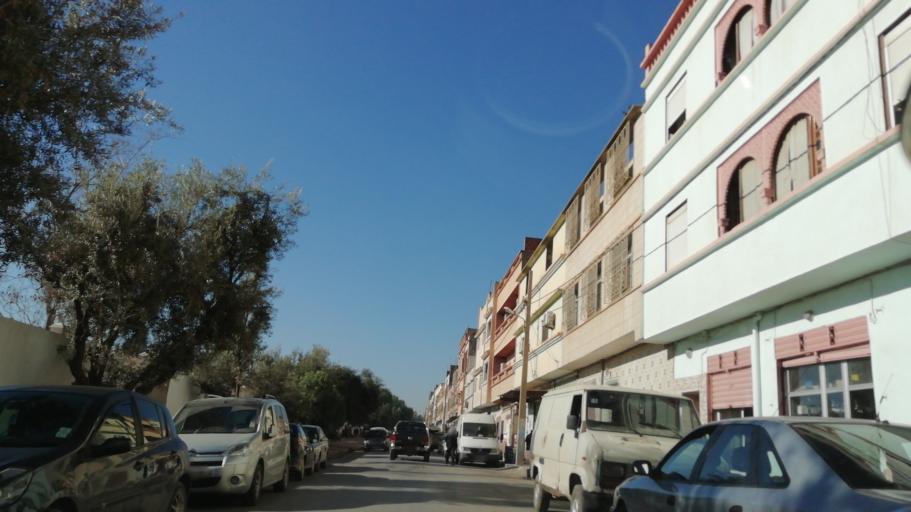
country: DZ
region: Tlemcen
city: Nedroma
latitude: 34.8472
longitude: -1.7397
